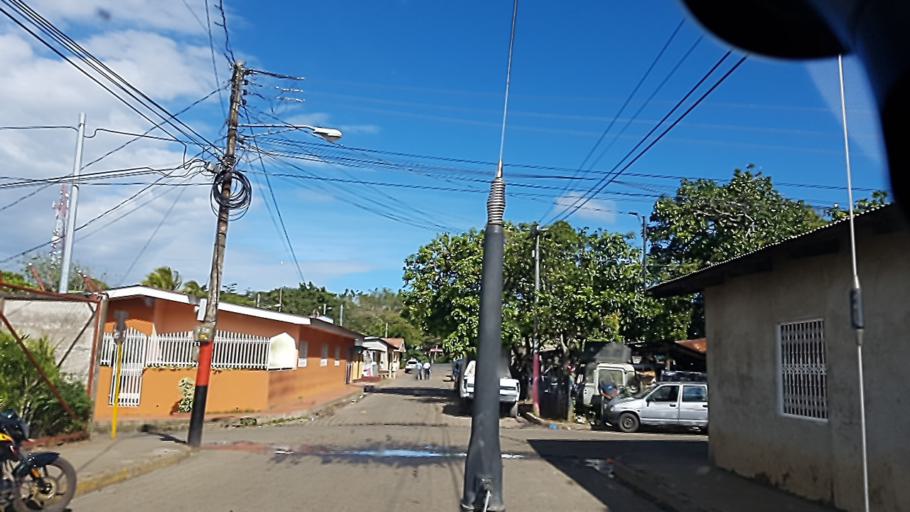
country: NI
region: Carazo
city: Dolores
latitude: 11.8574
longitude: -86.2157
